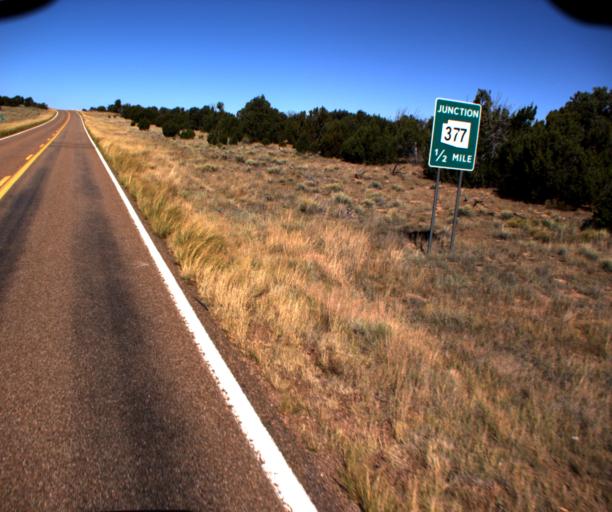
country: US
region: Arizona
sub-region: Navajo County
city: Heber-Overgaard
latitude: 34.4611
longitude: -110.4700
